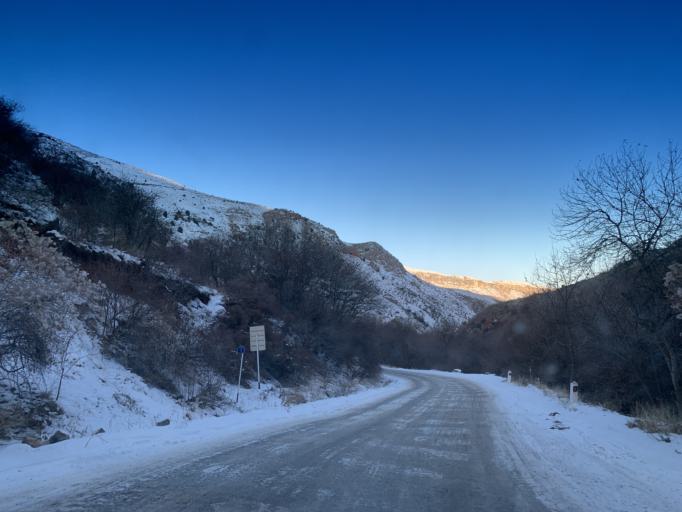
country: AM
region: Vayots' Dzori Marz
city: Areni
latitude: 39.6822
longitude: 45.2348
